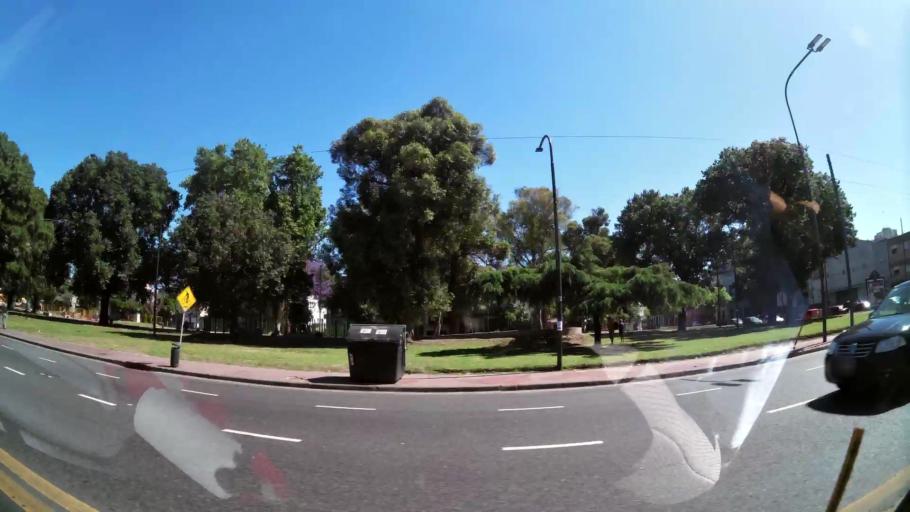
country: AR
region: Buenos Aires F.D.
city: Buenos Aires
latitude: -34.6271
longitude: -58.3876
